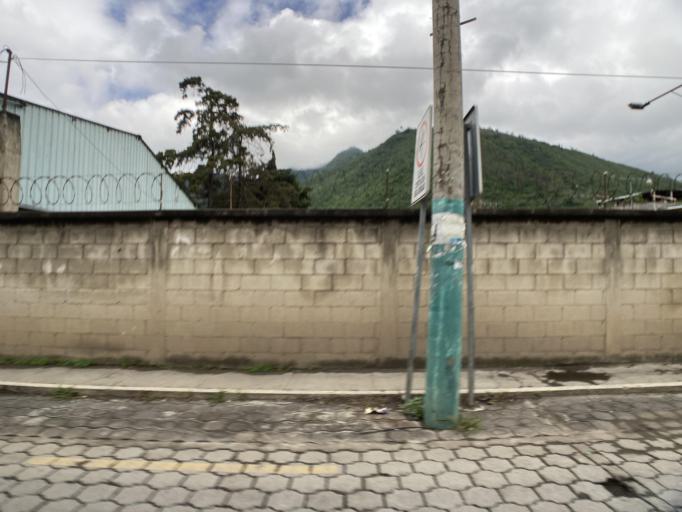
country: GT
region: Sacatepequez
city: Jocotenango
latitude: 14.5783
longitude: -90.7461
